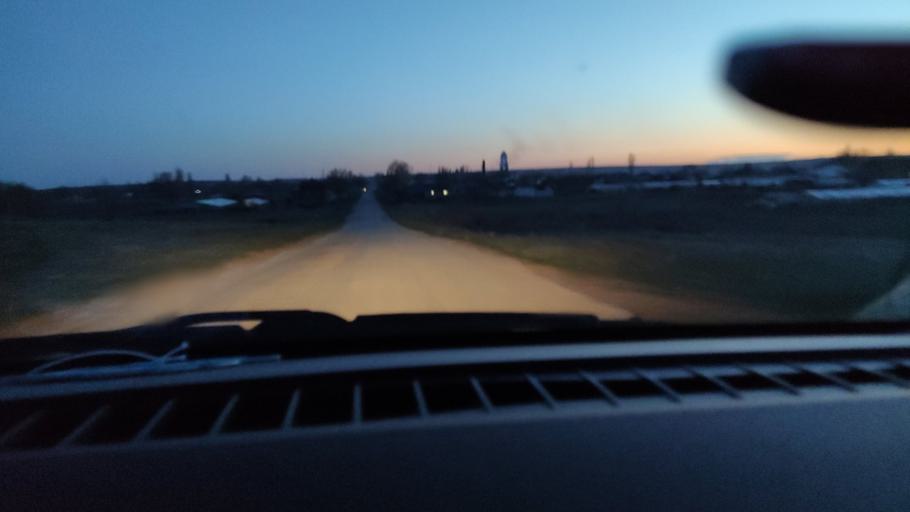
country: RU
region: Saratov
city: Rovnoye
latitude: 50.9294
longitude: 46.0852
